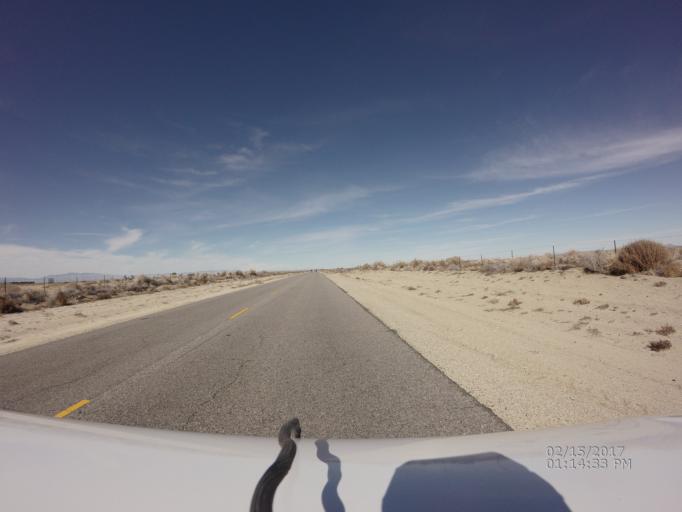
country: US
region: California
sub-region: Los Angeles County
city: Littlerock
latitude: 34.6229
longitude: -118.0053
